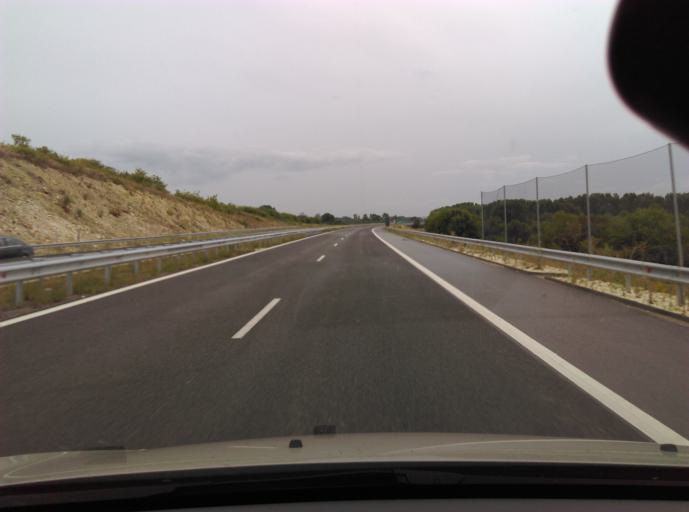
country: BG
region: Stara Zagora
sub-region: Obshtina Chirpan
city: Chirpan
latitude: 42.0952
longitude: 25.4386
